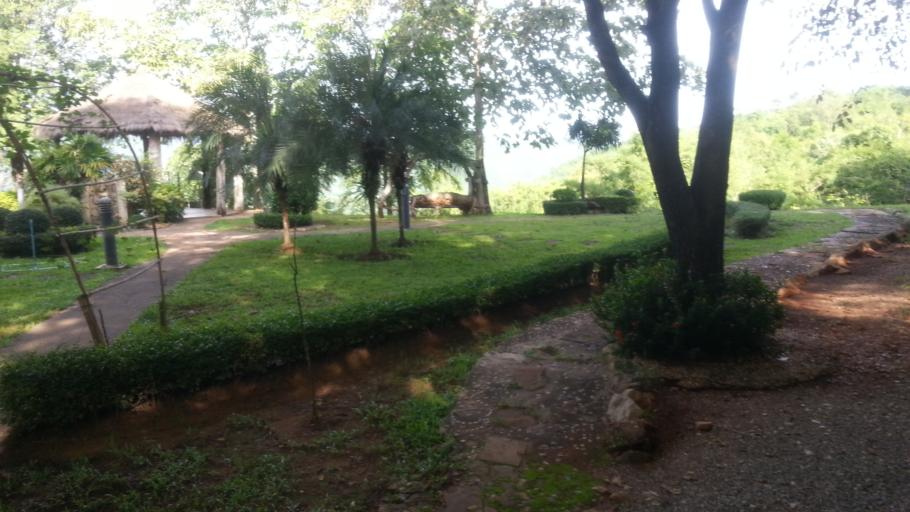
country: TH
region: Kanchanaburi
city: Sai Yok
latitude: 14.1179
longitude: 99.1525
